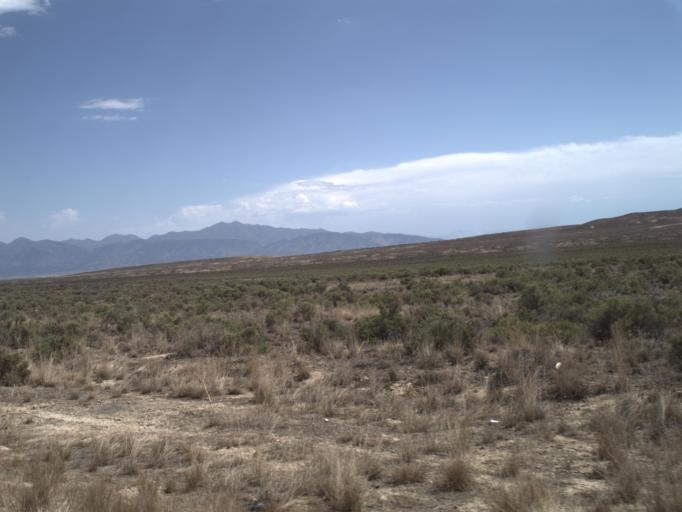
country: US
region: Utah
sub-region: Tooele County
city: Tooele
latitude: 40.1309
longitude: -112.4308
